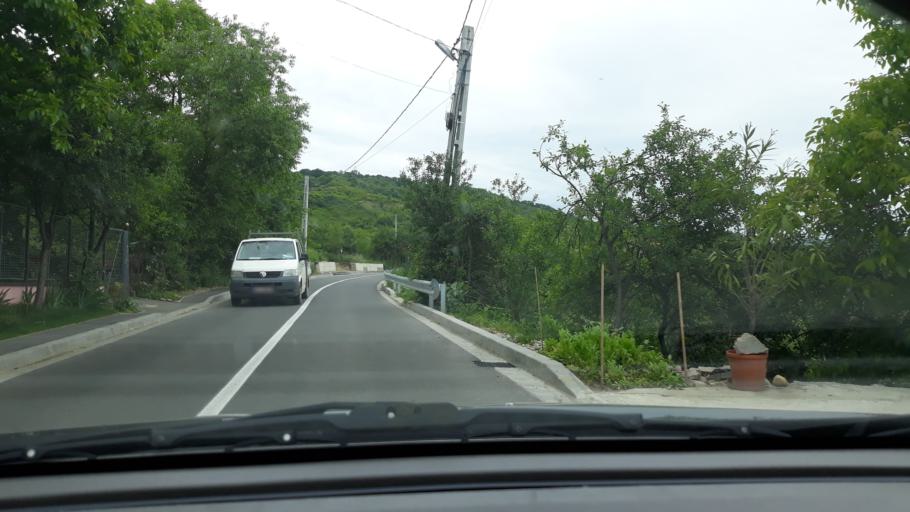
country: RO
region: Bihor
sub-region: Comuna Osorheiu
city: Osorheiu
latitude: 47.0633
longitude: 22.0295
